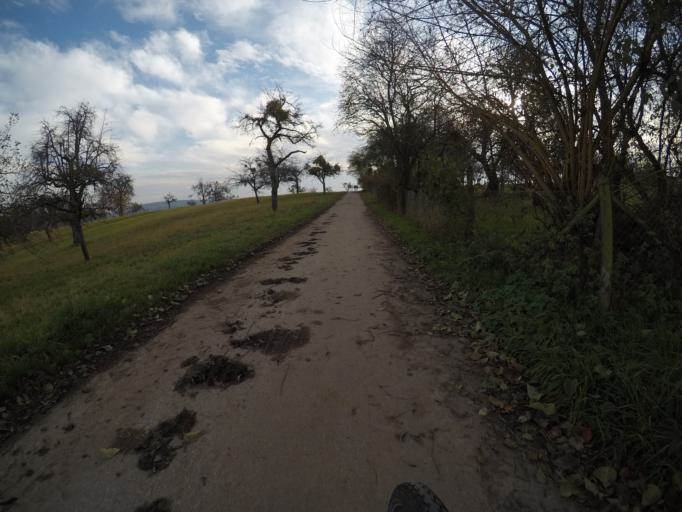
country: DE
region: Baden-Wuerttemberg
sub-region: Regierungsbezirk Stuttgart
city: Steinenbronn
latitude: 48.7006
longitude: 9.1209
